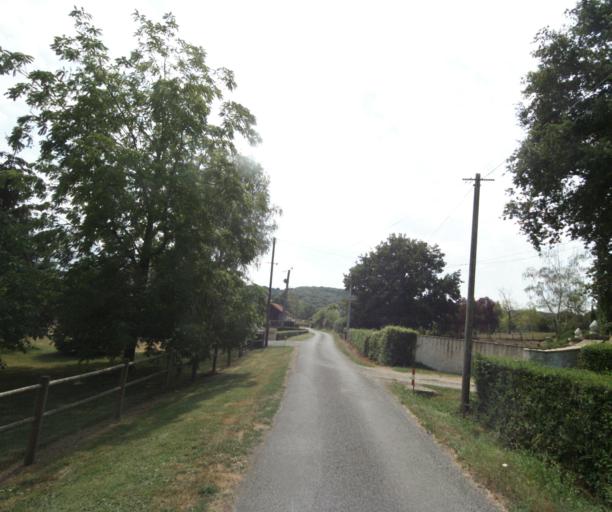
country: FR
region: Bourgogne
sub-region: Departement de Saone-et-Loire
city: Gueugnon
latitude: 46.6151
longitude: 4.0437
